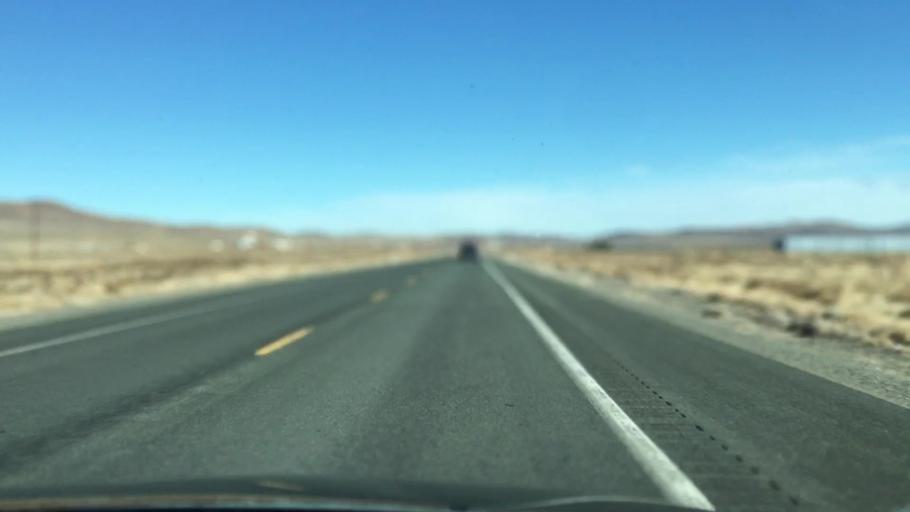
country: US
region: Nevada
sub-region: Lyon County
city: Silver Springs
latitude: 39.4060
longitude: -119.2527
